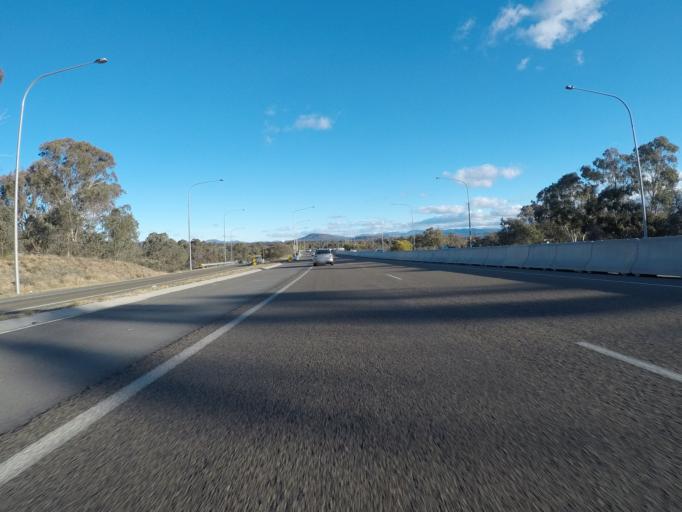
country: AU
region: Australian Capital Territory
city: Acton
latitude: -35.2788
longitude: 149.0867
